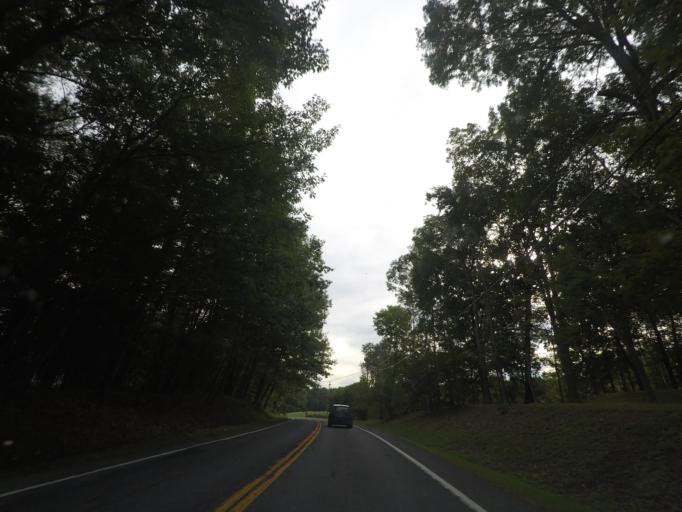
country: US
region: New York
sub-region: Rensselaer County
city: West Sand Lake
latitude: 42.5841
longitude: -73.6227
